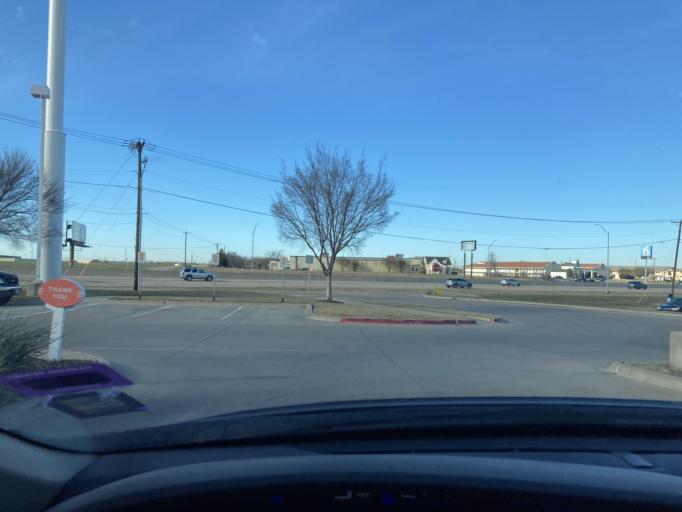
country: US
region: Texas
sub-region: Navarro County
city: Corsicana
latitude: 32.0703
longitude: -96.4475
